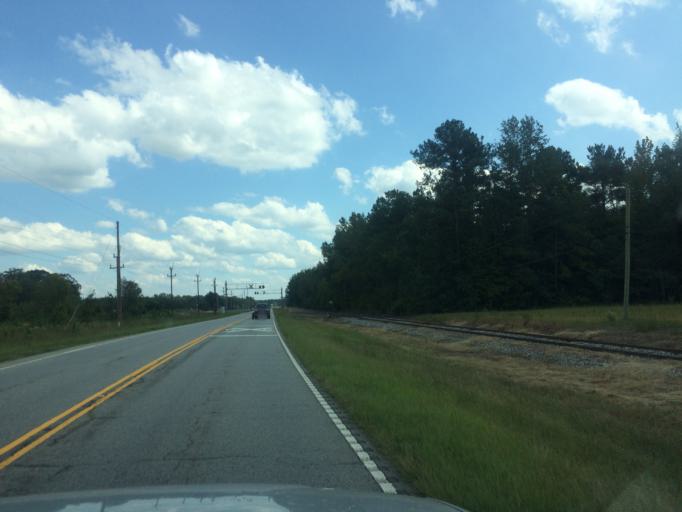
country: US
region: South Carolina
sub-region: Anderson County
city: Belton
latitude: 34.5058
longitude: -82.4708
